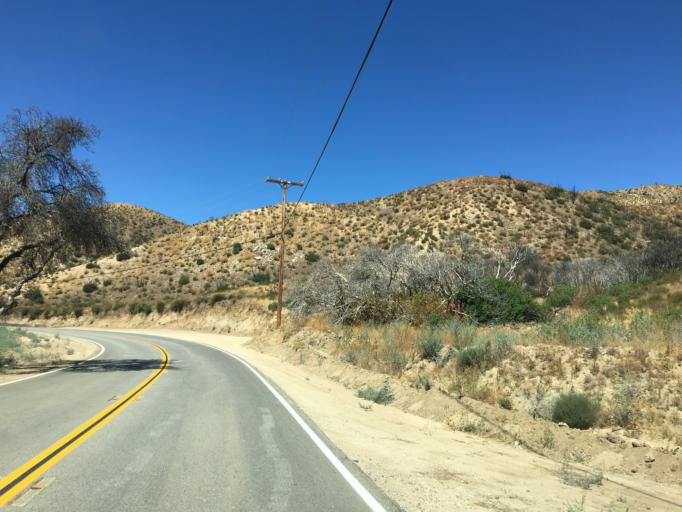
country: US
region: California
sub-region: Los Angeles County
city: Green Valley
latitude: 34.6620
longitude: -118.4581
